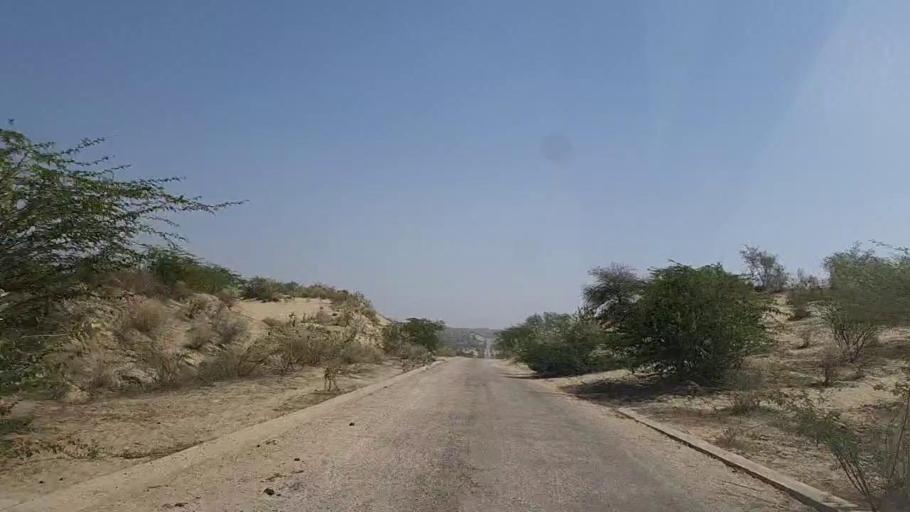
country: PK
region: Sindh
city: Diplo
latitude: 24.5137
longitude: 69.3916
